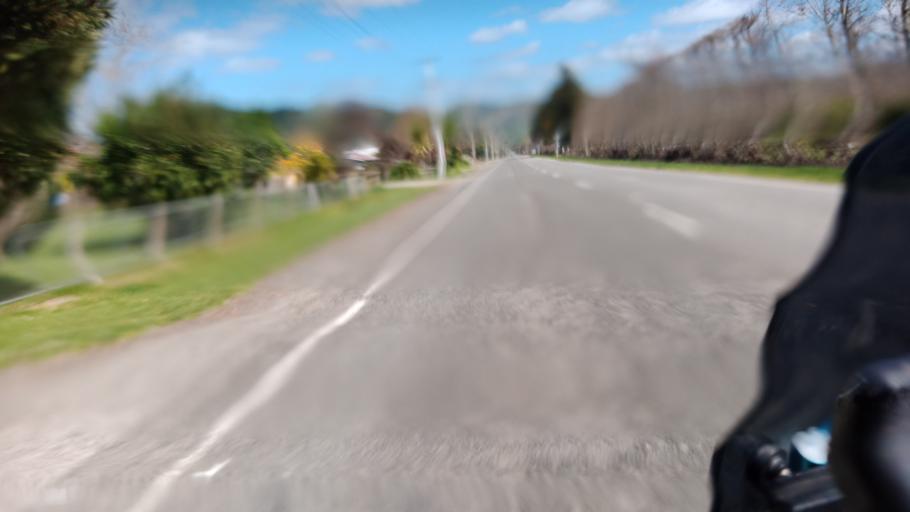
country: NZ
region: Gisborne
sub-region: Gisborne District
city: Gisborne
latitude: -38.6796
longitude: 177.9035
